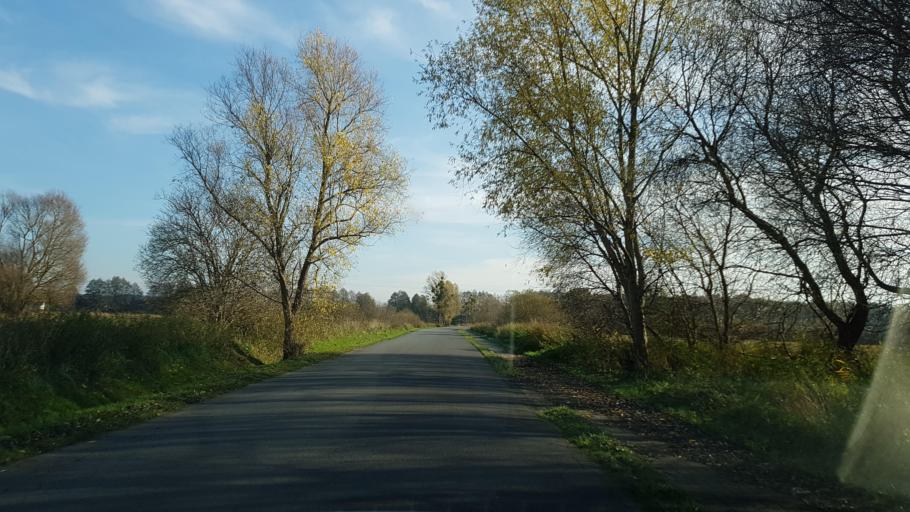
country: PL
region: West Pomeranian Voivodeship
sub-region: Powiat policki
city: Dobra
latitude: 53.4955
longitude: 14.3666
